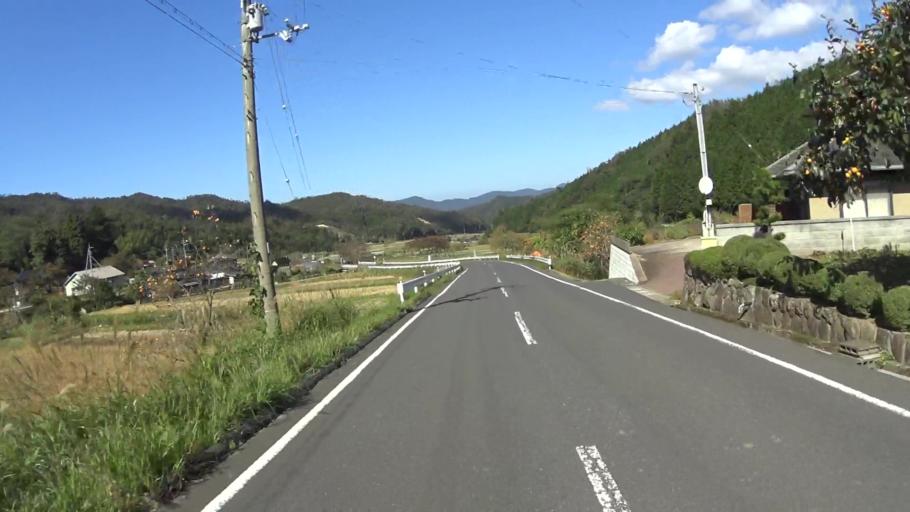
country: JP
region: Hyogo
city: Toyooka
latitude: 35.5466
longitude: 134.9785
